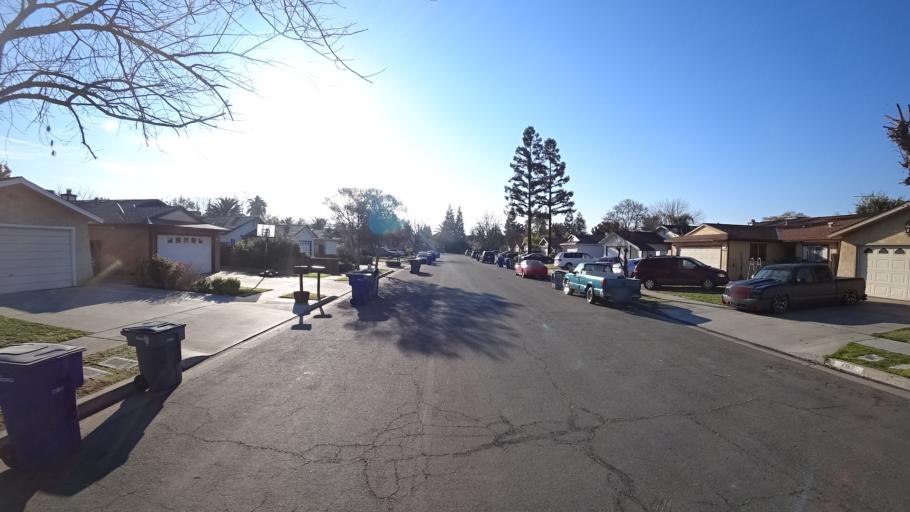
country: US
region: California
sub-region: Fresno County
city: West Park
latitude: 36.8164
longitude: -119.8705
